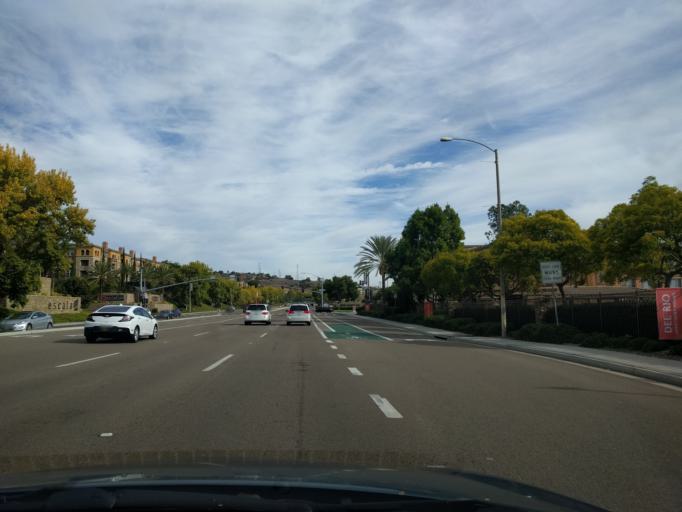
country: US
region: California
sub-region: San Diego County
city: San Diego
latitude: 32.7804
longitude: -117.1323
